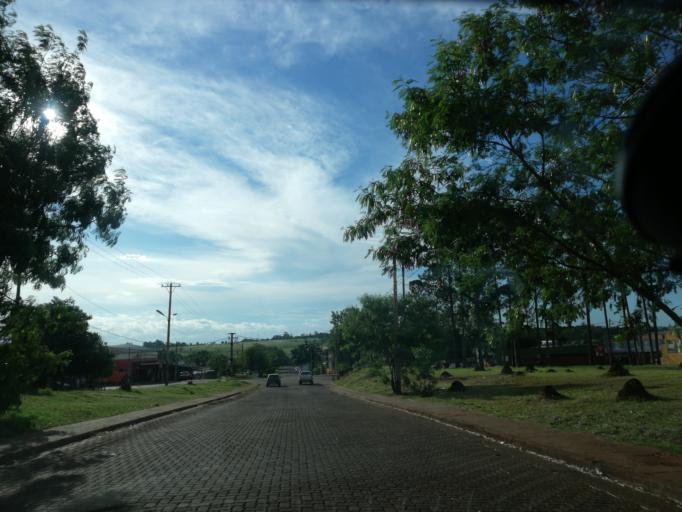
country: AR
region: Misiones
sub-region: Departamento de Capital
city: Posadas
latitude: -27.4148
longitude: -55.9552
